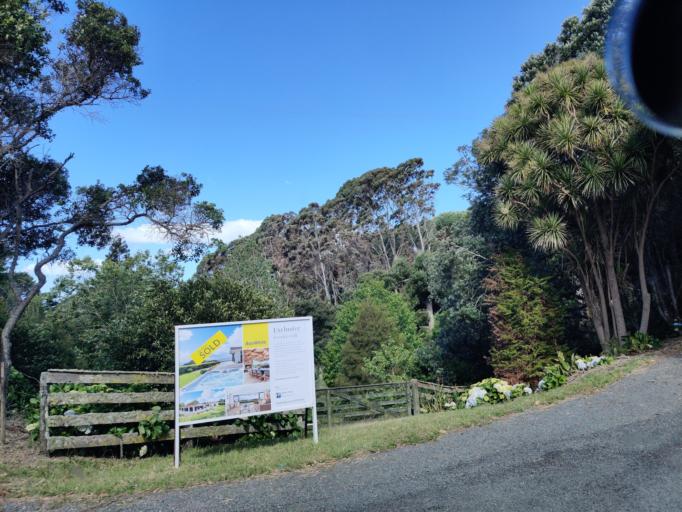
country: NZ
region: Northland
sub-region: Whangarei
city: Ngunguru
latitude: -35.6057
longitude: 174.5249
